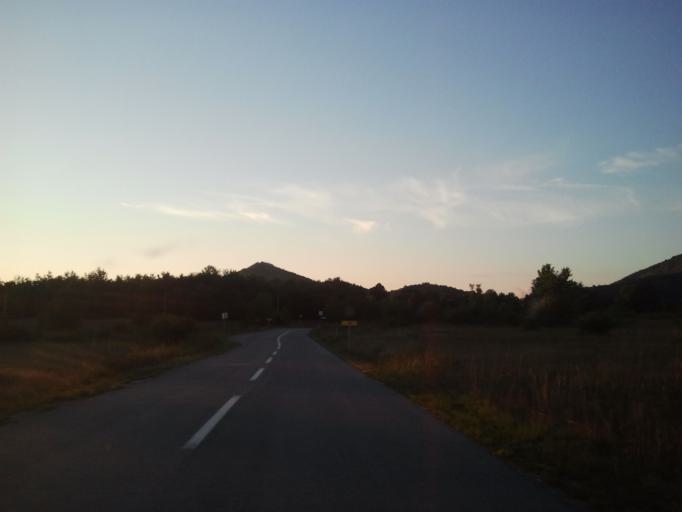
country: HR
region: Zadarska
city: Obrovac
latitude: 44.4189
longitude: 15.6613
